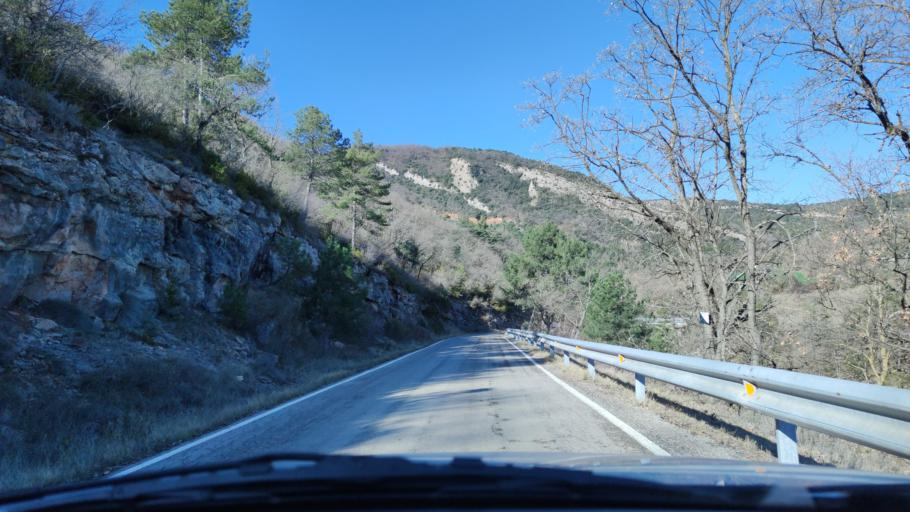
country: ES
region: Catalonia
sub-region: Provincia de Lleida
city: Llimiana
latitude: 42.0448
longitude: 1.0401
